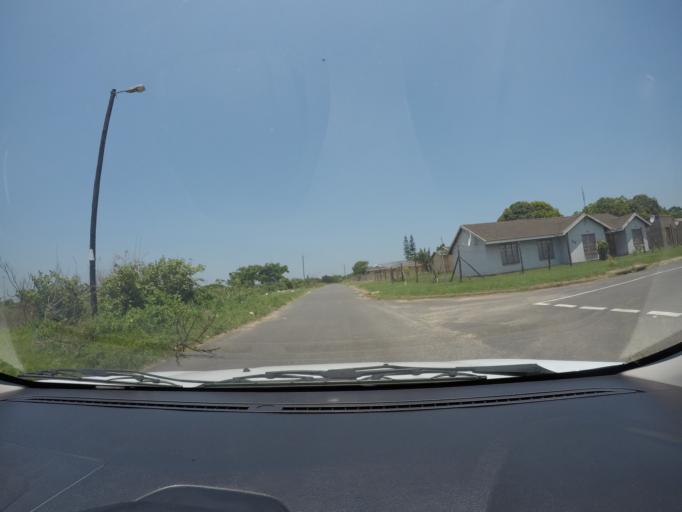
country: ZA
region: KwaZulu-Natal
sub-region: uThungulu District Municipality
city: eSikhawini
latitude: -28.8794
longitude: 31.8937
